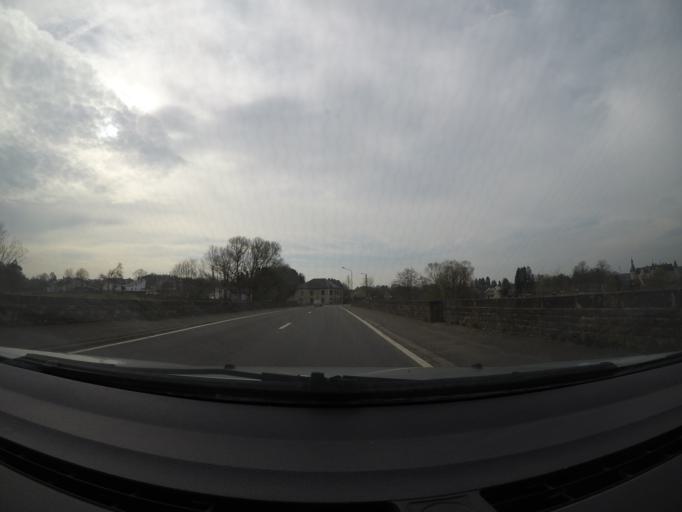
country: BE
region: Wallonia
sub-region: Province du Luxembourg
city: Chiny
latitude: 49.6972
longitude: 5.4141
